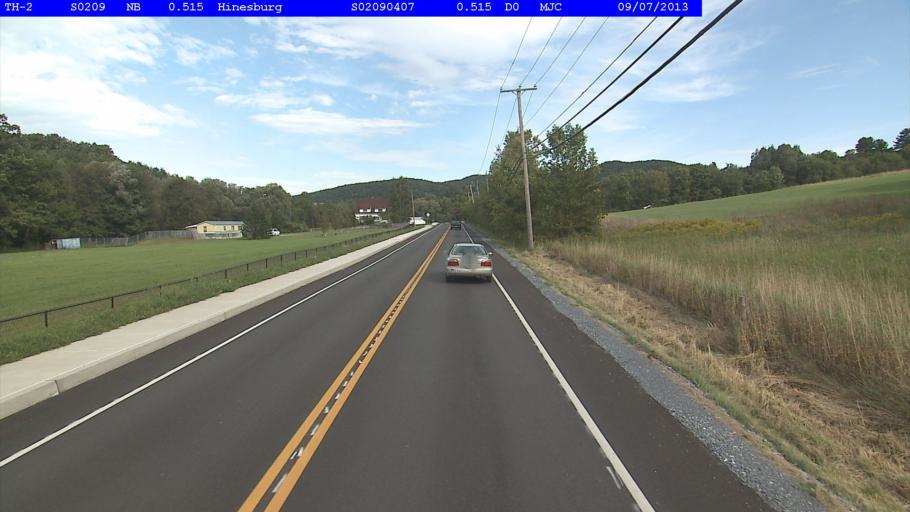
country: US
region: Vermont
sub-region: Chittenden County
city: Hinesburg
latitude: 44.3378
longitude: -73.1055
